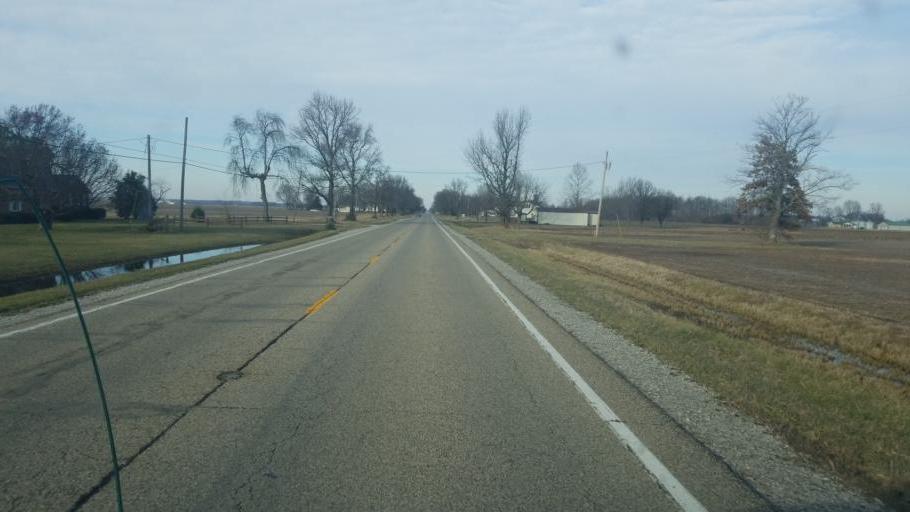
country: US
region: Illinois
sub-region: Lawrence County
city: Bridgeport
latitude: 38.5821
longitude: -87.6945
